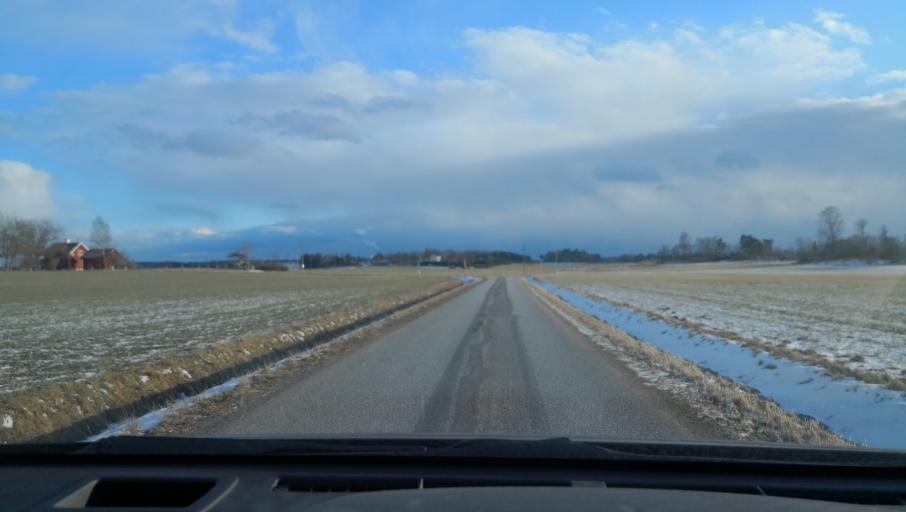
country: SE
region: Uppsala
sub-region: Enkopings Kommun
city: Irsta
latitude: 59.6910
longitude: 16.8593
